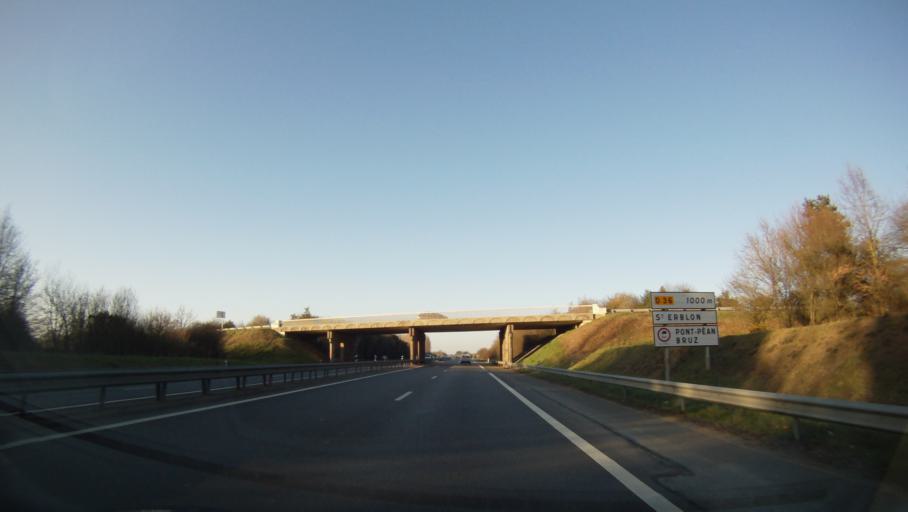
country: FR
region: Brittany
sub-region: Departement d'Ille-et-Vilaine
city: Orgeres
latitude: 48.0064
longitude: -1.6921
